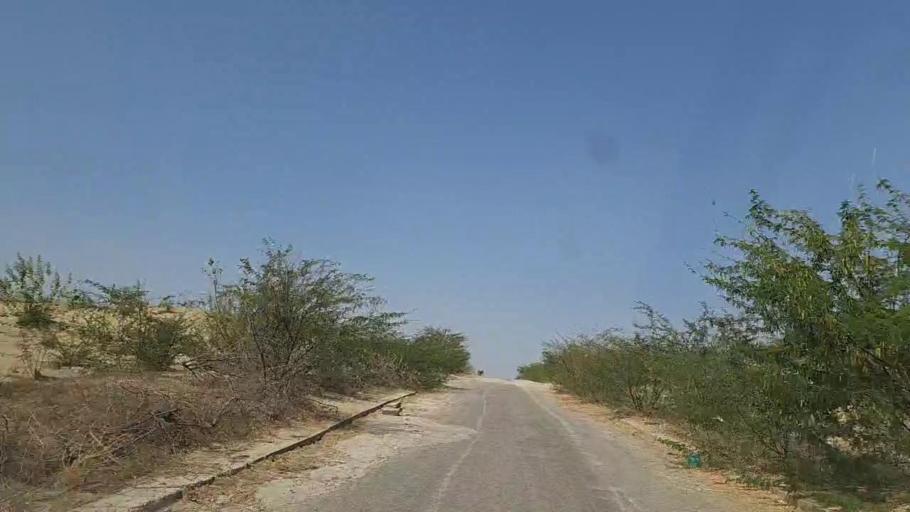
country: PK
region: Sindh
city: Naukot
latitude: 24.5881
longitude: 69.3171
